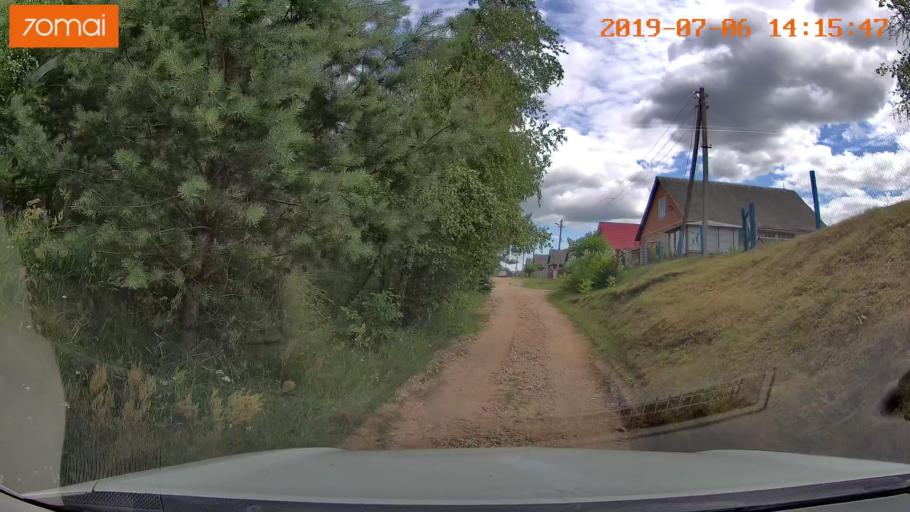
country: BY
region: Minsk
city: Ivyanyets
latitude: 53.8932
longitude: 26.7376
